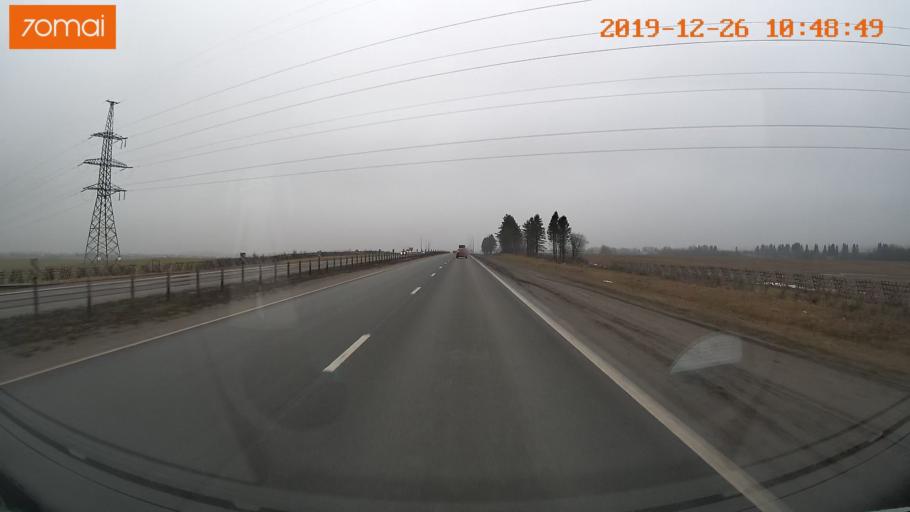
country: RU
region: Vologda
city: Molochnoye
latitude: 59.2119
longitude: 39.7315
